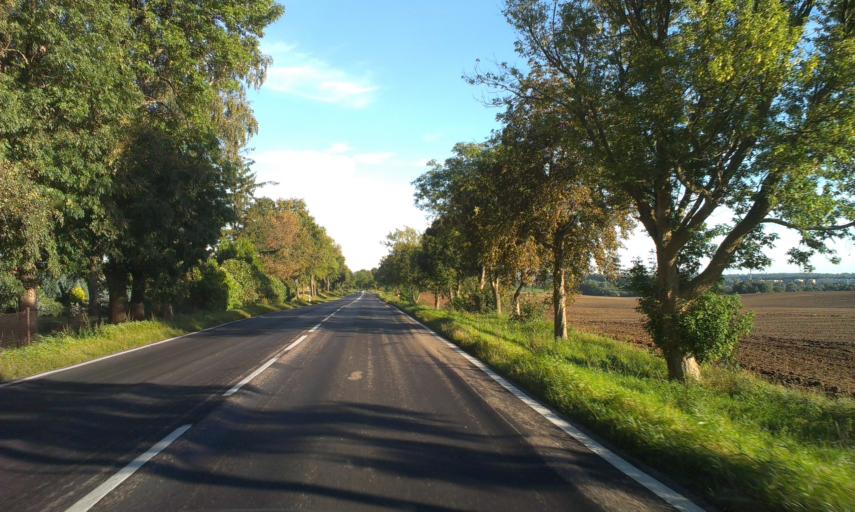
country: PL
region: West Pomeranian Voivodeship
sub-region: Powiat szczecinecki
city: Szczecinek
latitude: 53.7402
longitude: 16.6635
